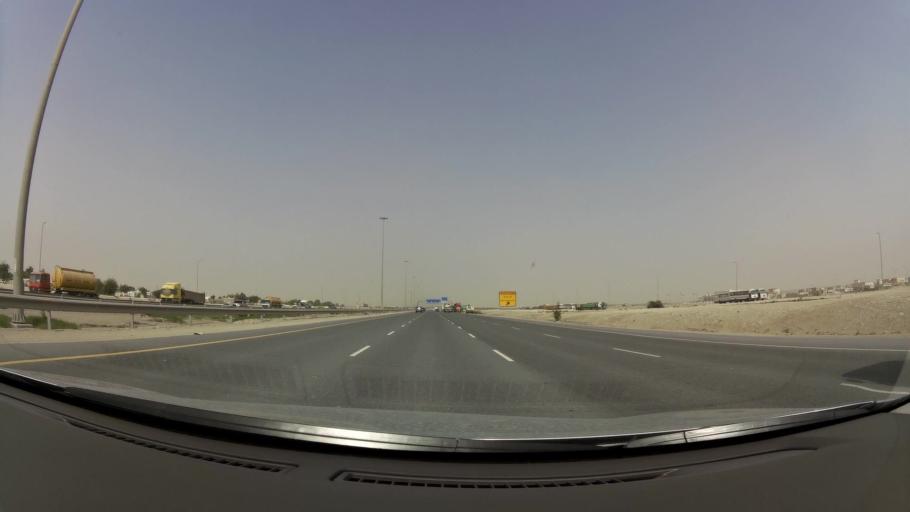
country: QA
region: Baladiyat ar Rayyan
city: Ar Rayyan
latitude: 25.1927
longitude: 51.3753
